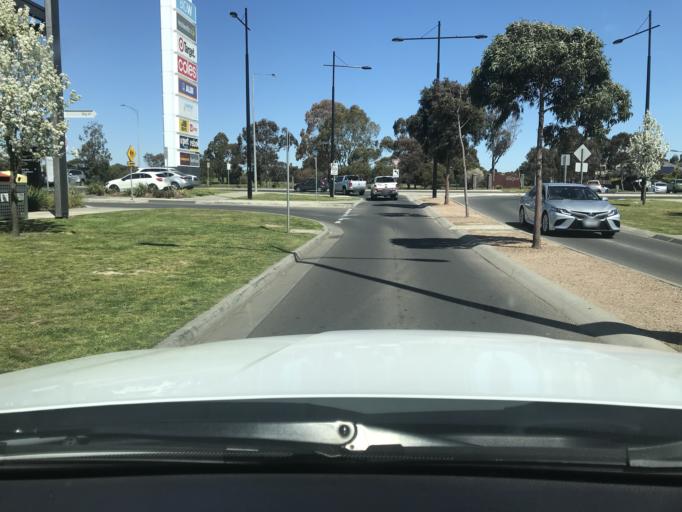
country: AU
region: Victoria
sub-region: Hume
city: Roxburgh Park
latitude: -37.5945
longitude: 144.9140
